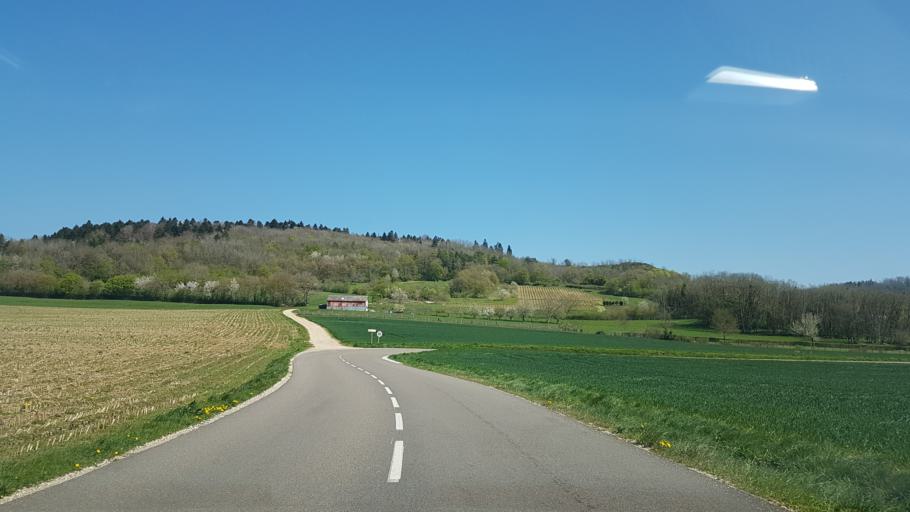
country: FR
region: Franche-Comte
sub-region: Departement du Jura
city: Saint-Amour
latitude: 46.4592
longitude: 5.3584
